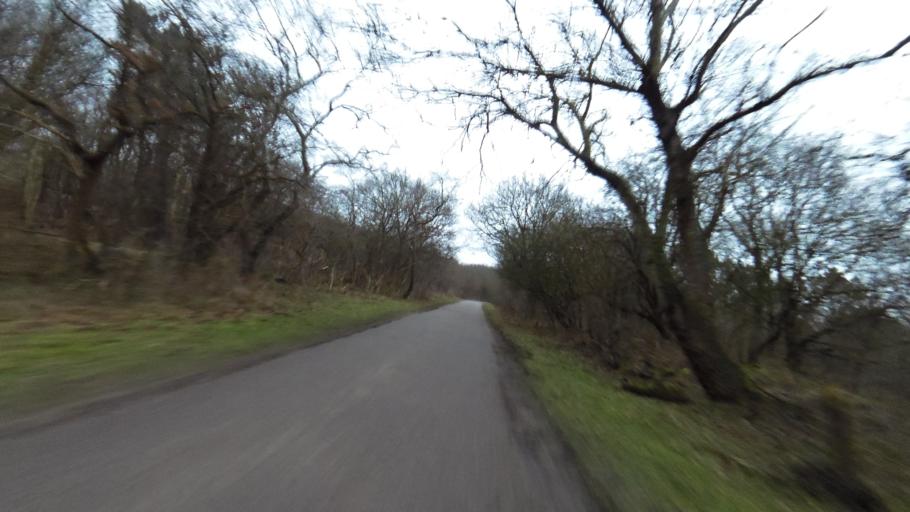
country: NL
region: North Holland
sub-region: Gemeente Castricum
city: Castricum
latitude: 52.5502
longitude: 4.6321
